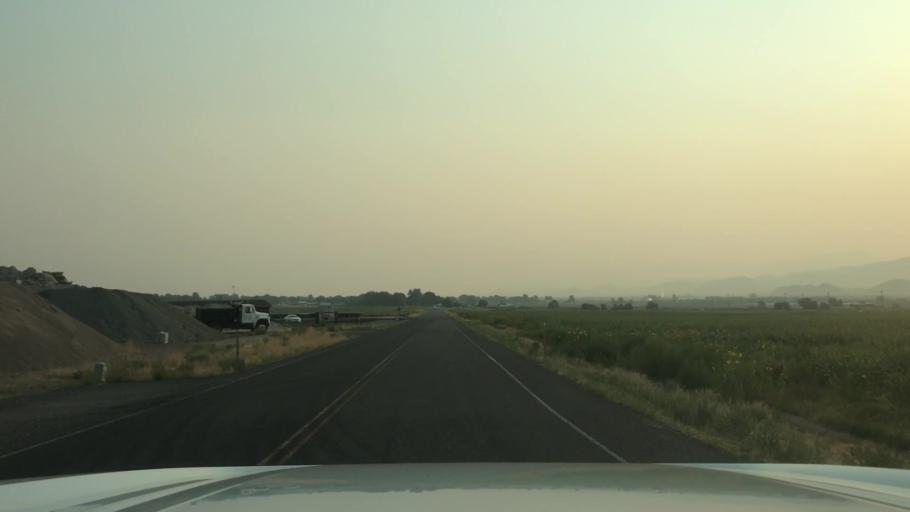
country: US
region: Utah
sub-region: Sevier County
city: Aurora
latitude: 38.9024
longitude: -111.9463
